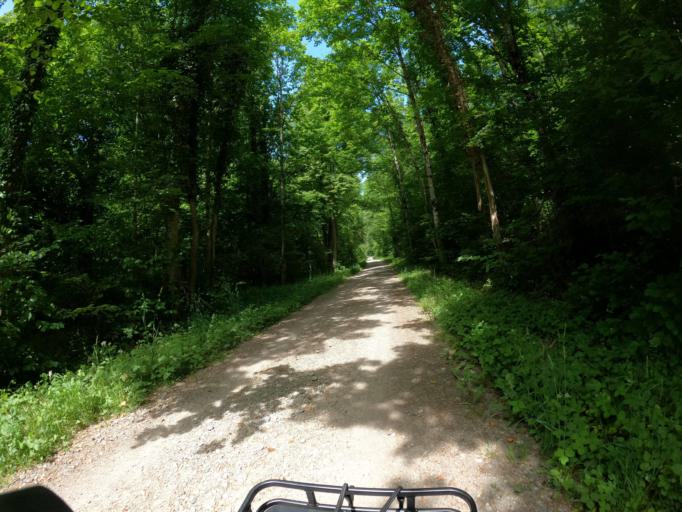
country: DE
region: Baden-Wuerttemberg
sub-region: Freiburg Region
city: Lottstetten
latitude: 47.6184
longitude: 8.6053
